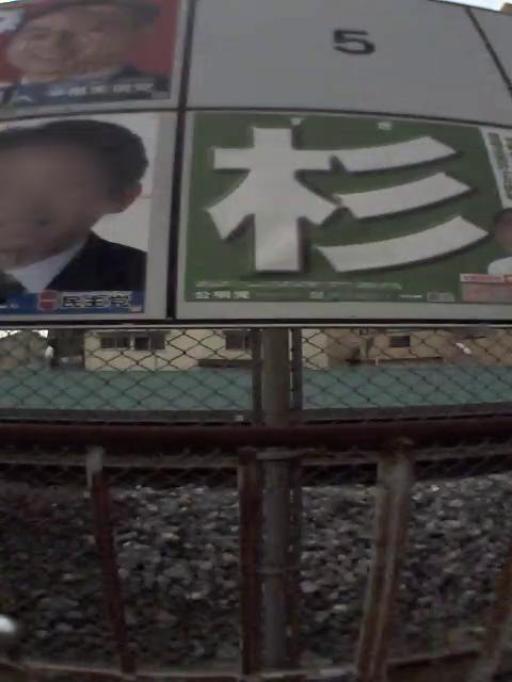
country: JP
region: Osaka
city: Hirakata
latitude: 34.8282
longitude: 135.6530
